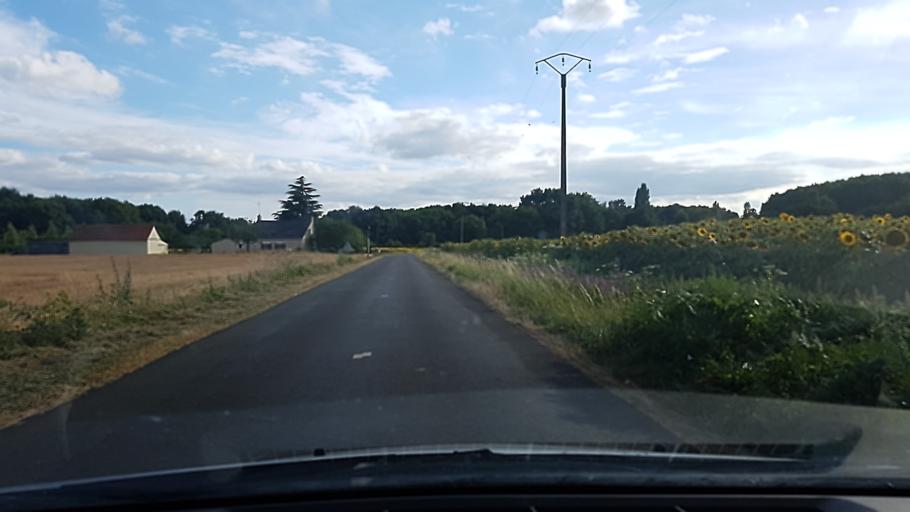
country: FR
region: Pays de la Loire
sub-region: Departement de Maine-et-Loire
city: Jarze
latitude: 47.5197
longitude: -0.2134
